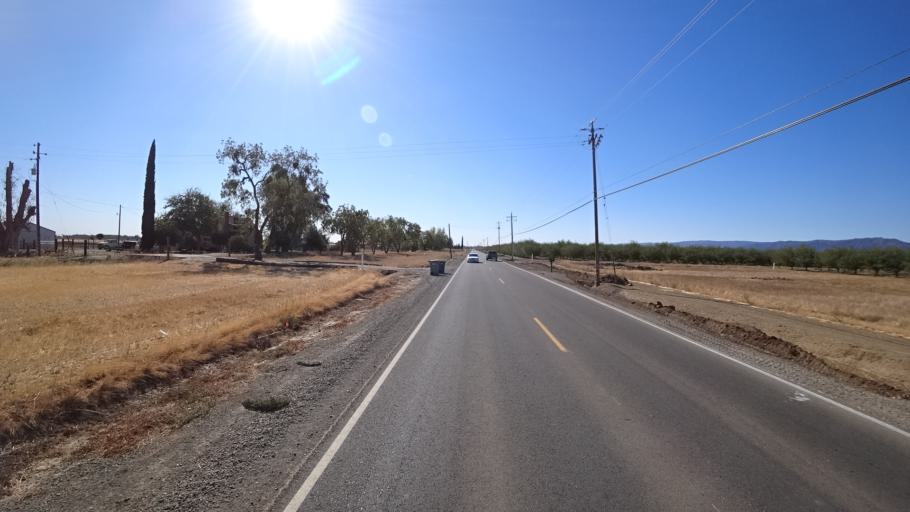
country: US
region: California
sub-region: Yolo County
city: Winters
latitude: 38.5539
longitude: -121.9712
